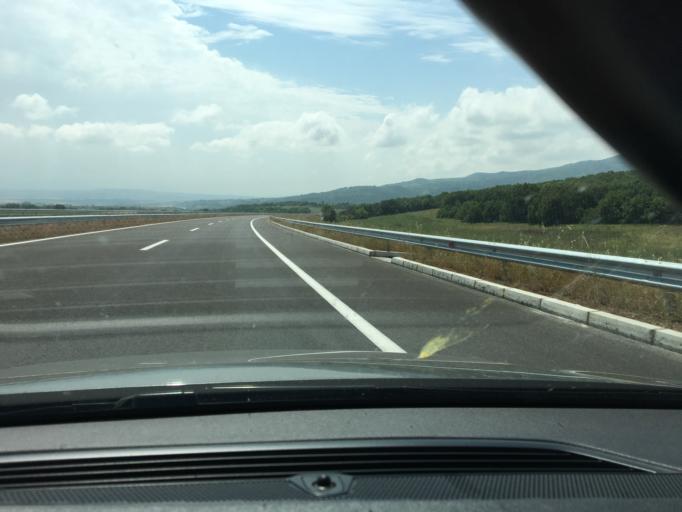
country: MK
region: Sveti Nikole
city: Gorobinci
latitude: 41.9381
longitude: 21.8192
